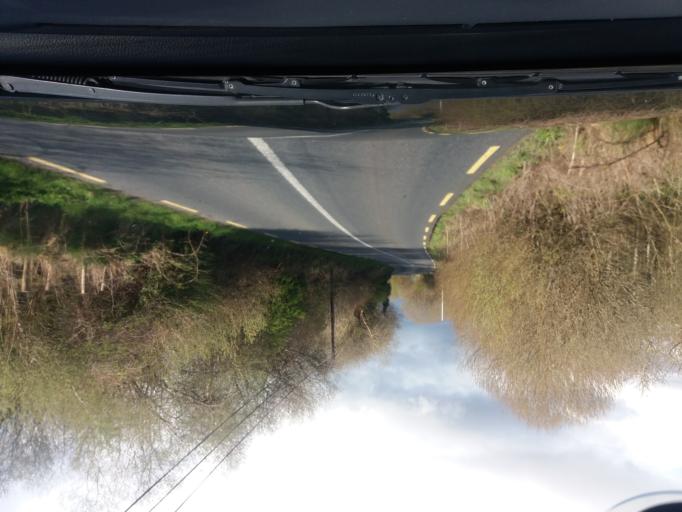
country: IE
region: Connaught
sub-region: County Leitrim
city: Manorhamilton
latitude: 54.3441
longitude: -8.2342
